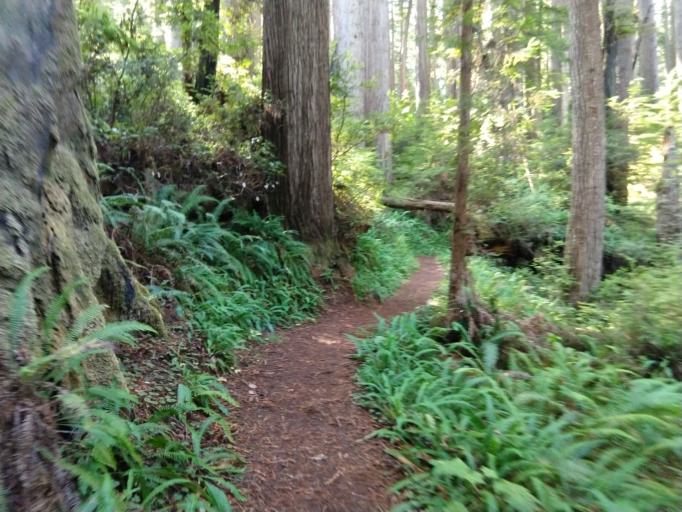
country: US
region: California
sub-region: Humboldt County
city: Westhaven-Moonstone
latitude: 41.3888
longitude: -124.0495
